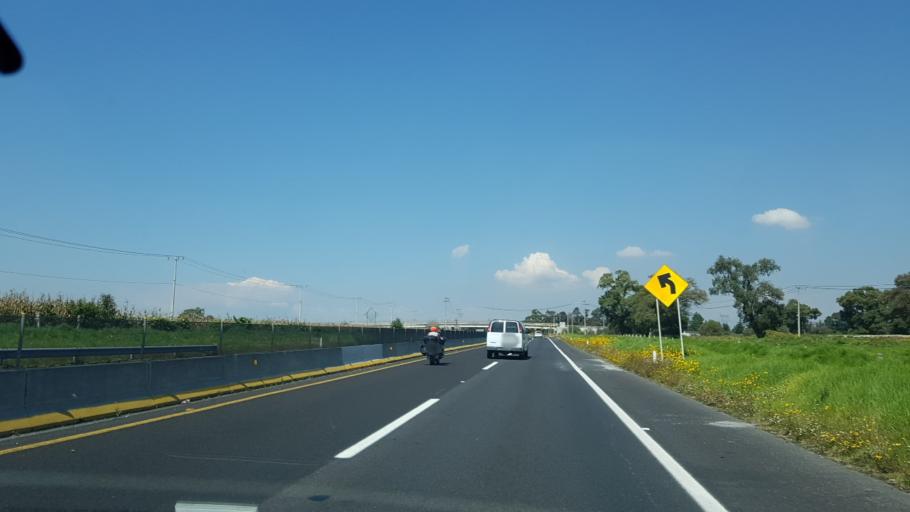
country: MX
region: Mexico
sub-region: Temoaya
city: Fraccionamiento Rinconada del Valle
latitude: 19.3930
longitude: -99.5693
